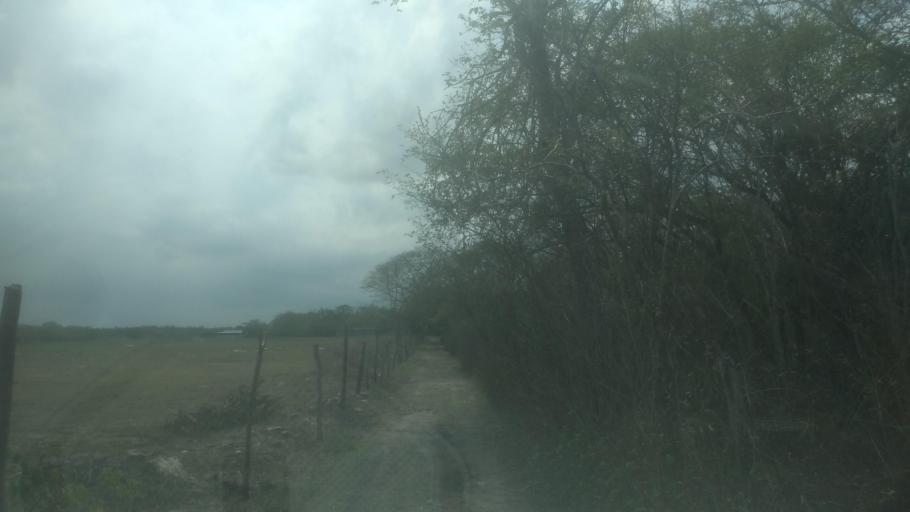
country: MX
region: Veracruz
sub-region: Emiliano Zapata
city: Plan del Rio
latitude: 19.3871
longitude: -96.6256
